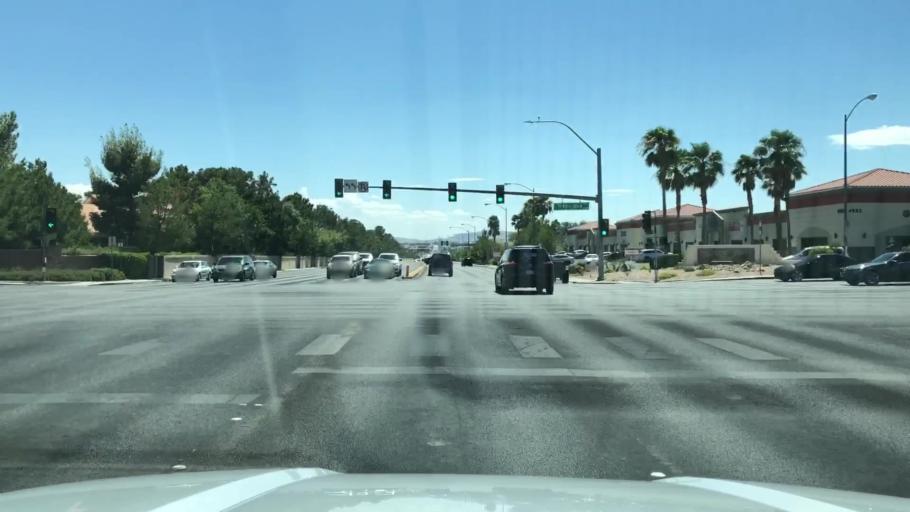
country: US
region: Nevada
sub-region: Clark County
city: Spring Valley
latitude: 36.1003
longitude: -115.2794
